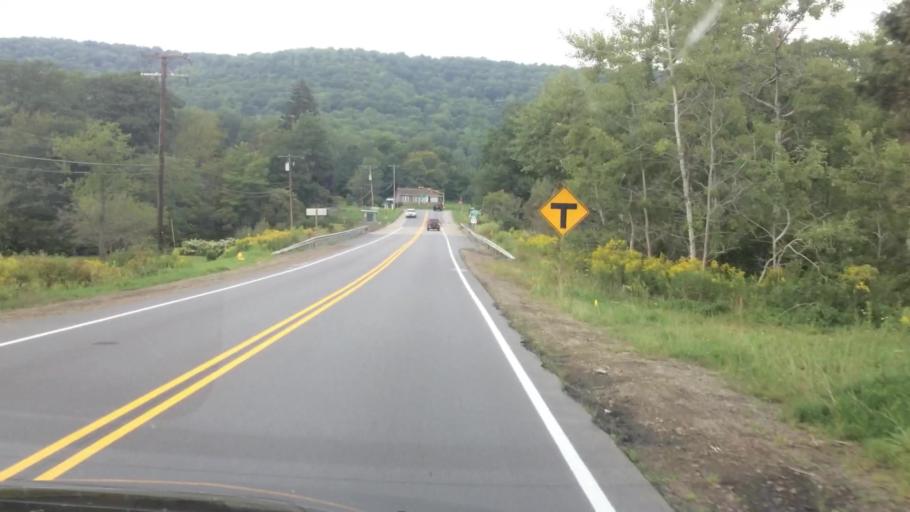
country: US
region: Pennsylvania
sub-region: McKean County
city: Bradford
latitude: 41.9143
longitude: -78.6483
